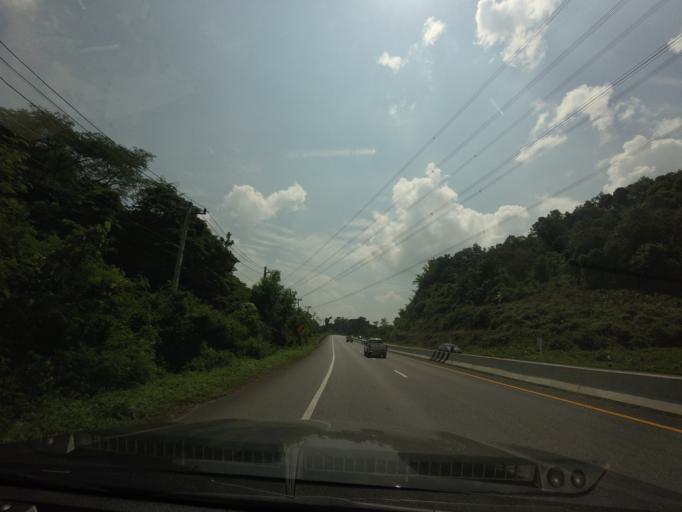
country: TH
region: Uttaradit
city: Uttaradit
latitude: 17.7691
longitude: 100.1318
